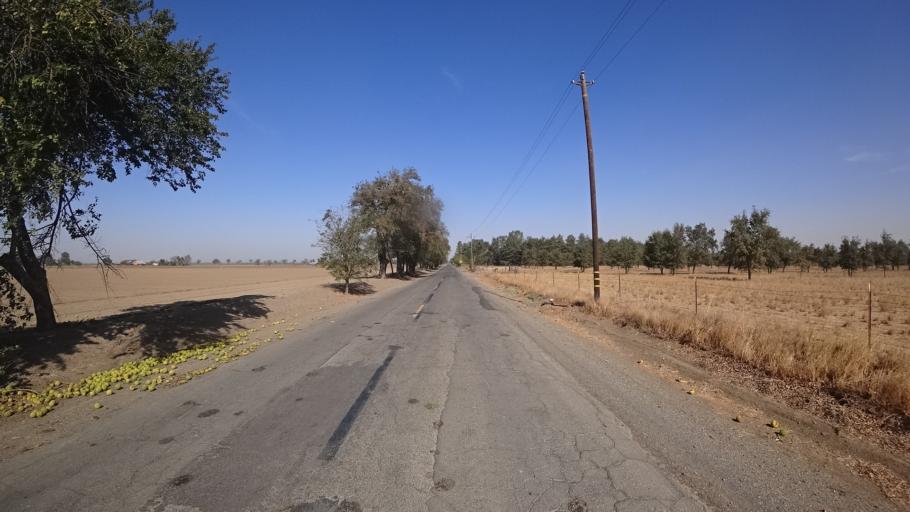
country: US
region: California
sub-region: Yolo County
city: Davis
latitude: 38.4896
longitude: -121.6957
